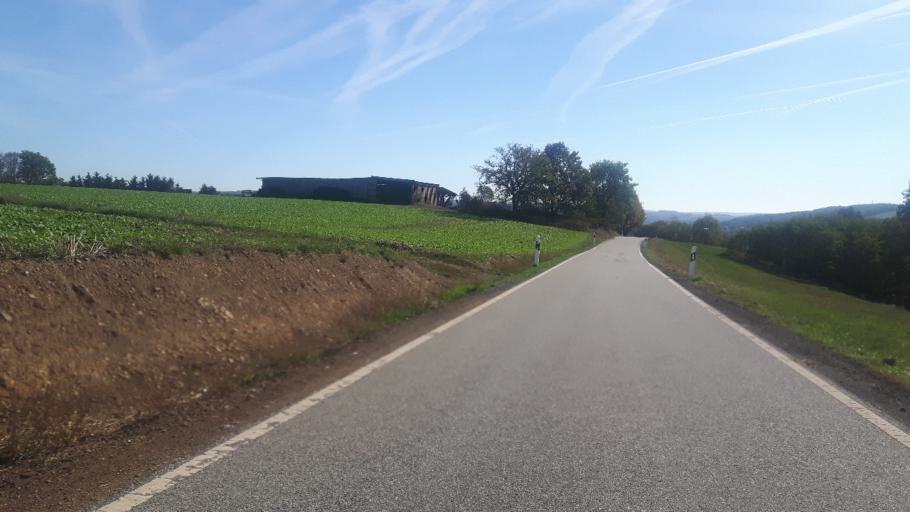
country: DE
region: Rheinland-Pfalz
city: Etzbach
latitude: 50.7856
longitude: 7.7003
